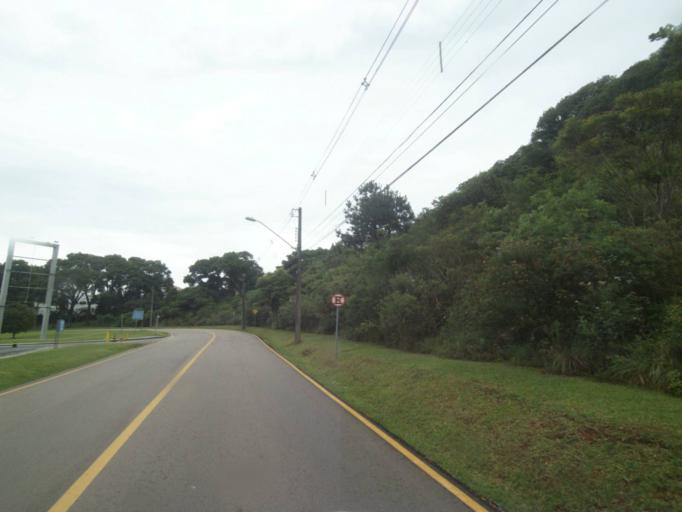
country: BR
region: Parana
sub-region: Curitiba
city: Curitiba
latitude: -25.4275
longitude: -49.3140
